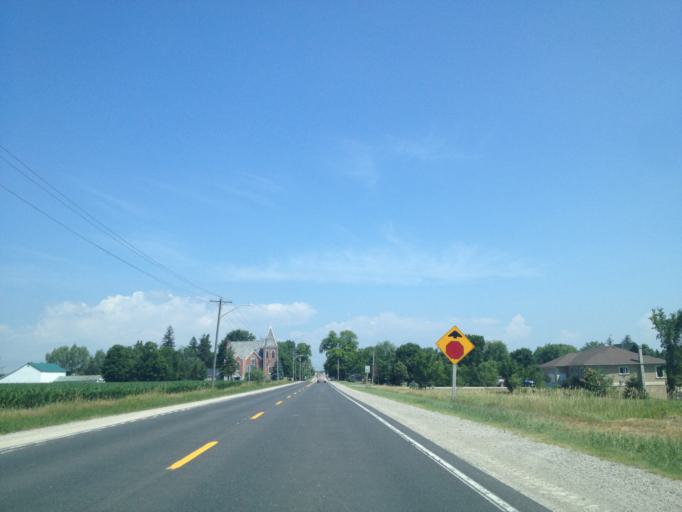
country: CA
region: Ontario
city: Huron East
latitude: 43.3866
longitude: -81.2212
